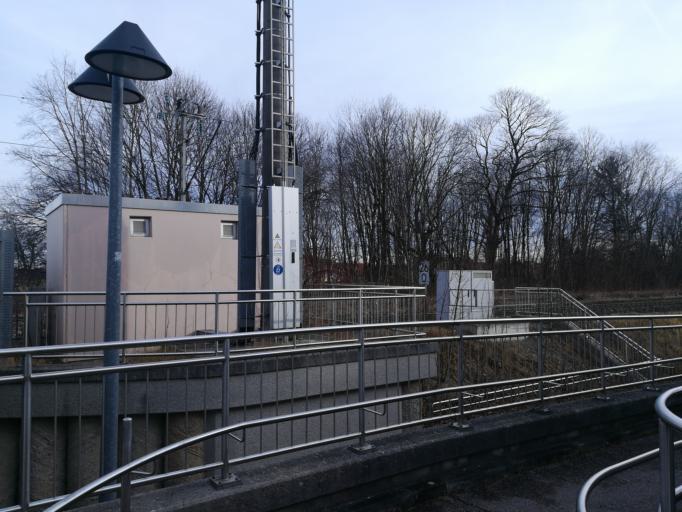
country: DE
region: Bavaria
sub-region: Upper Bavaria
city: Sauerlach
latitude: 47.9734
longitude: 11.6552
